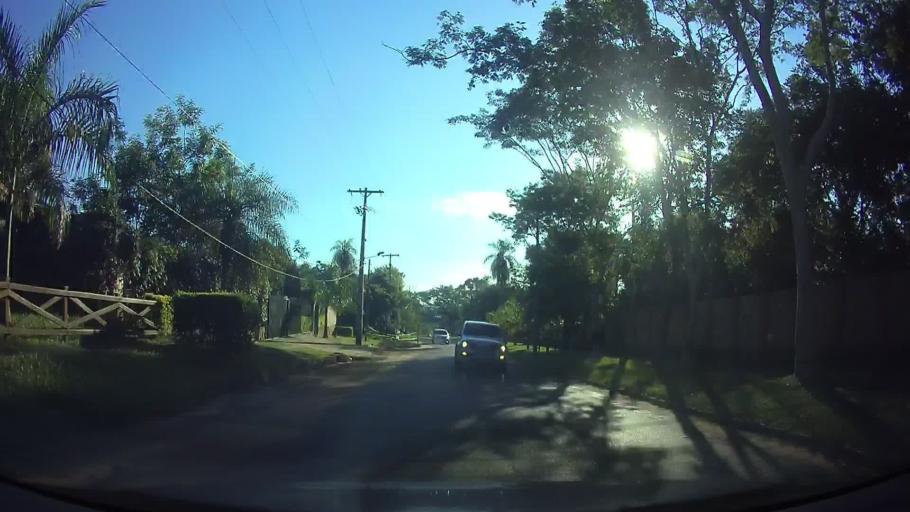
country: PY
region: Cordillera
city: San Bernardino
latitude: -25.3214
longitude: -57.2744
